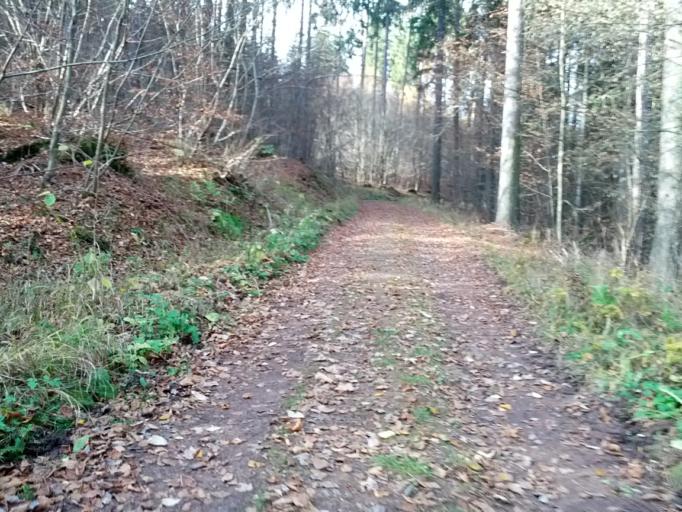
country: DE
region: Thuringia
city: Eisenach
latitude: 50.9499
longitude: 10.3469
